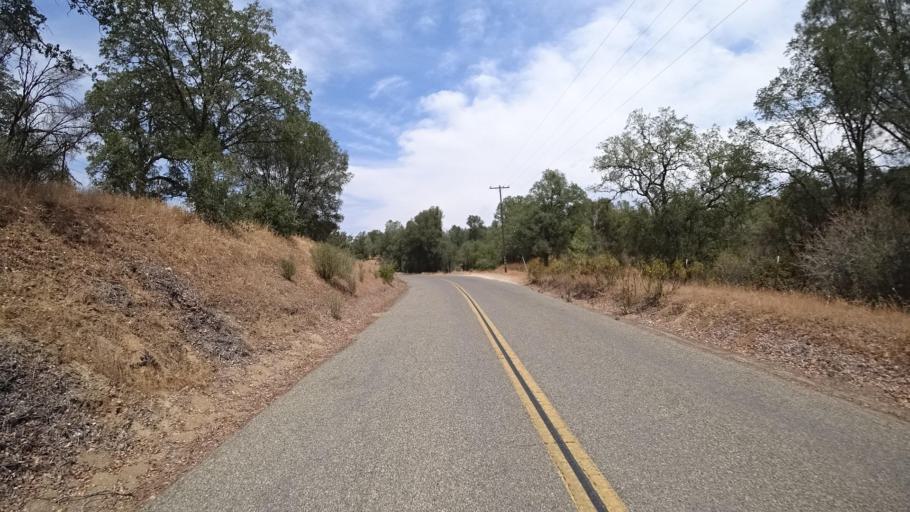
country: US
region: California
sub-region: Mariposa County
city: Mariposa
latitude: 37.4302
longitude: -119.8582
